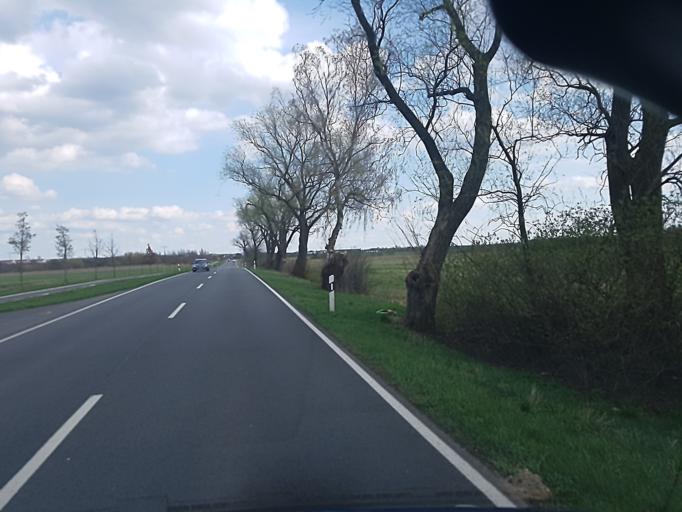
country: DE
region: Saxony-Anhalt
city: Grafenhainichen
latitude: 51.7400
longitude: 12.4293
